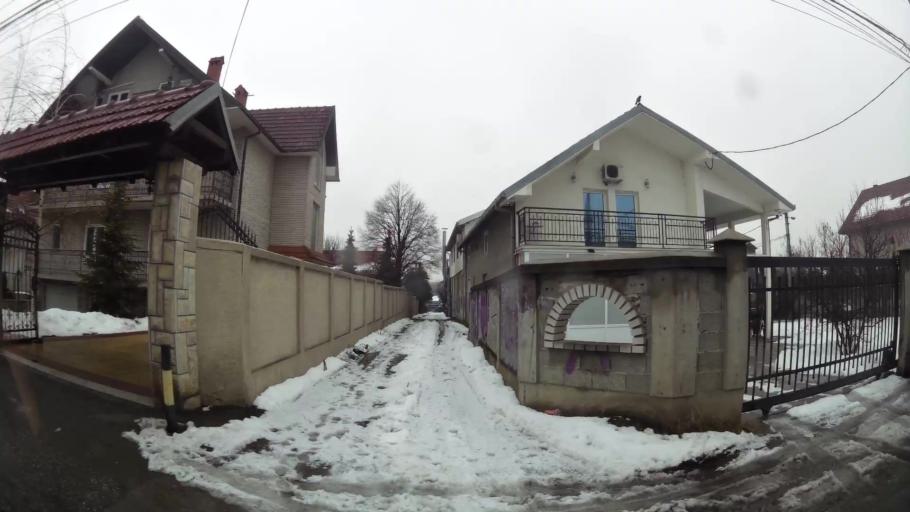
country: RS
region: Central Serbia
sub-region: Belgrade
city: Zemun
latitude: 44.8443
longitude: 20.3658
